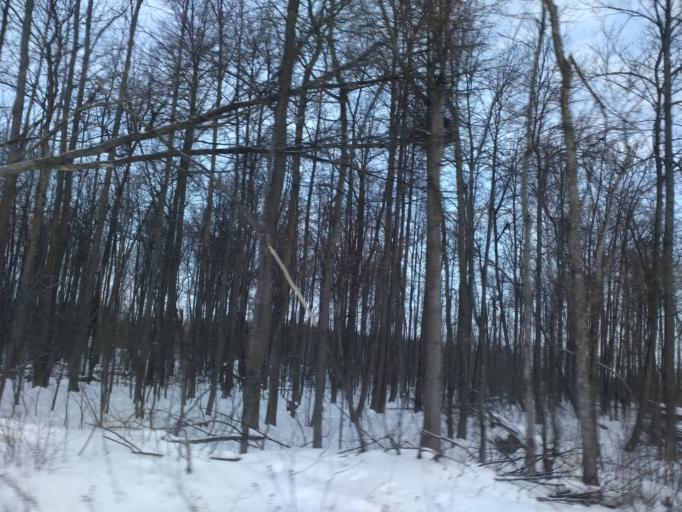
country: RU
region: Bashkortostan
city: Kudeyevskiy
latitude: 54.7120
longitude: 56.6521
